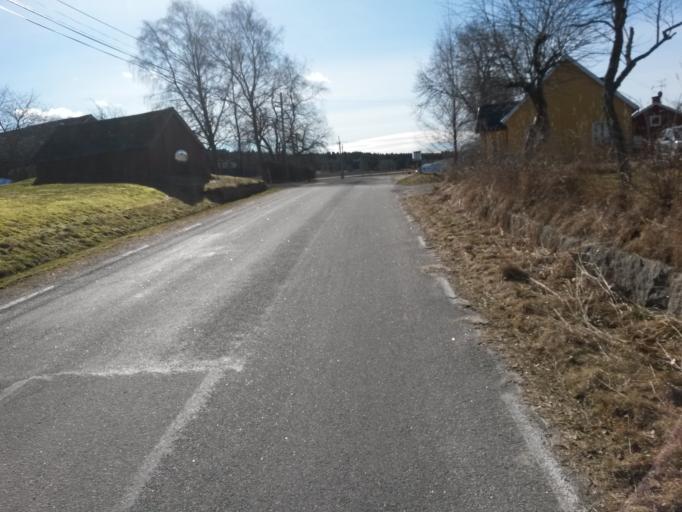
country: SE
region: Vaestra Goetaland
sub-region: Vargarda Kommun
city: Jonstorp
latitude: 57.9709
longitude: 12.6512
